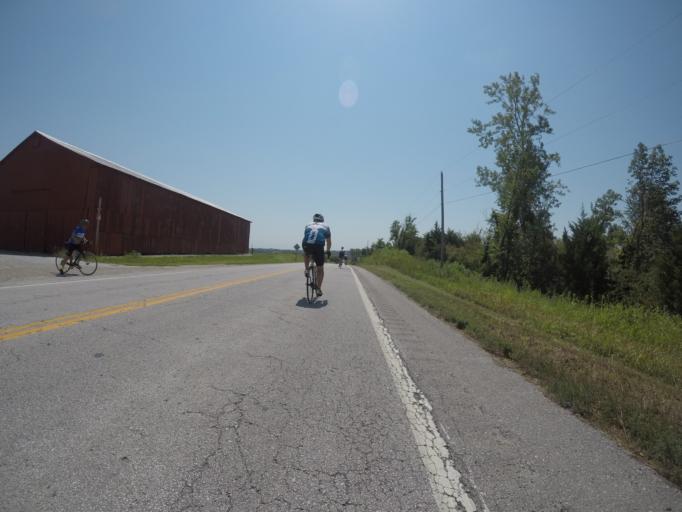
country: US
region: Missouri
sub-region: Platte County
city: Weston
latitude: 39.3968
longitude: -94.8632
